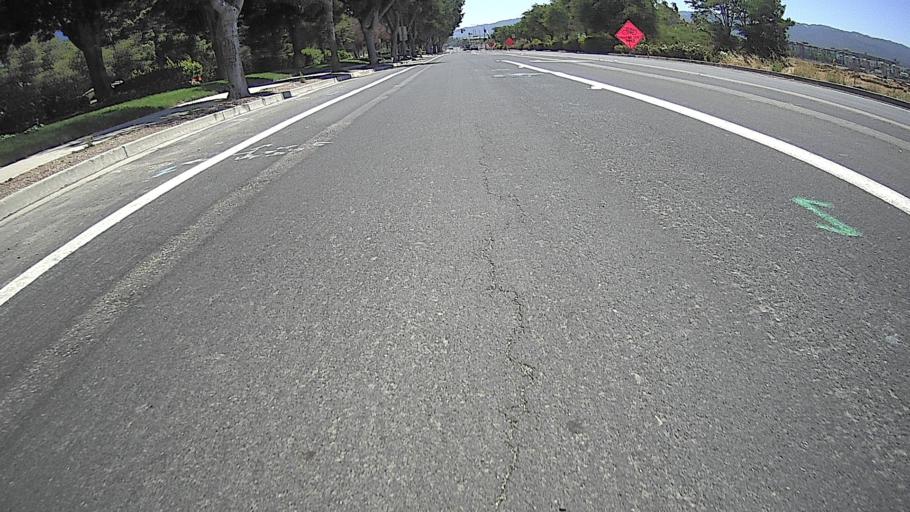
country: US
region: California
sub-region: Alameda County
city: Dublin
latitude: 37.7110
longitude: -121.8931
